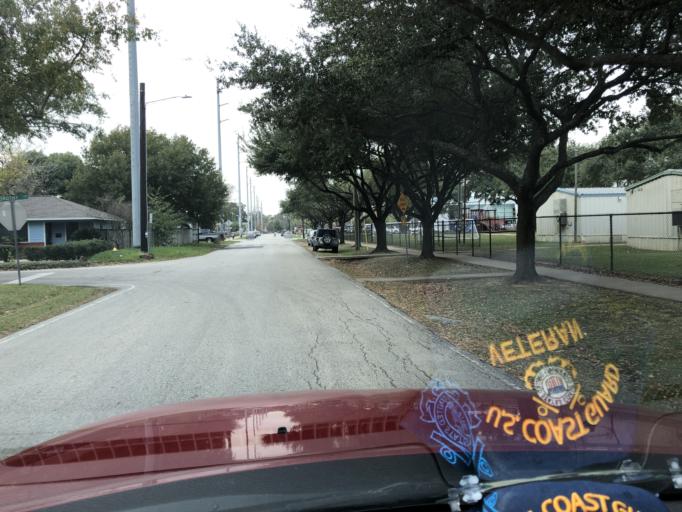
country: US
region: Texas
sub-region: Harris County
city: Houston
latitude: 29.7924
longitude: -95.4086
